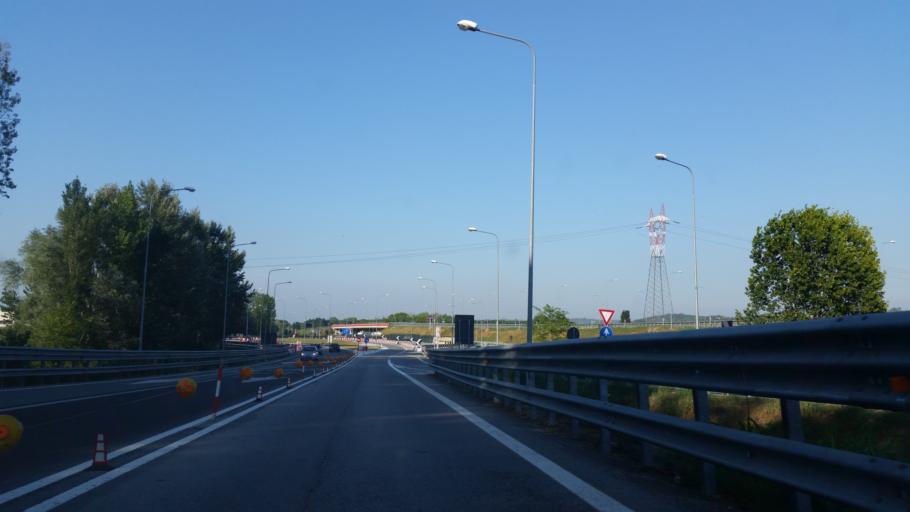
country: IT
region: Piedmont
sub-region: Provincia di Cuneo
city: Sant'Antonio
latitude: 44.7411
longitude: 8.0685
